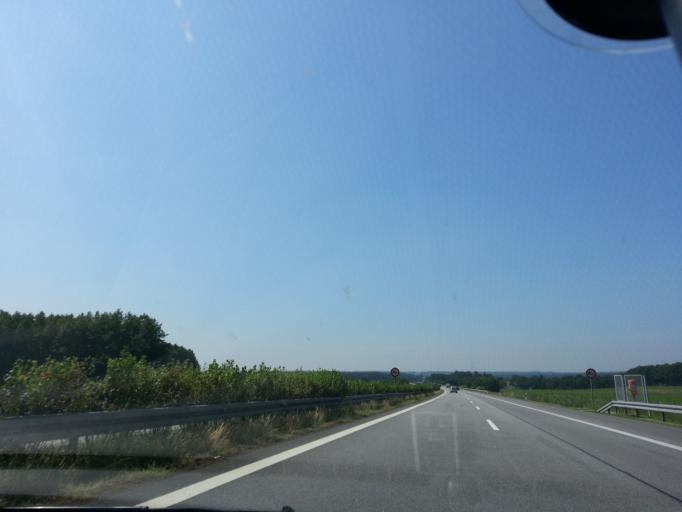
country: DE
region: Mecklenburg-Vorpommern
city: Neuburg
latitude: 53.3350
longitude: 11.8623
